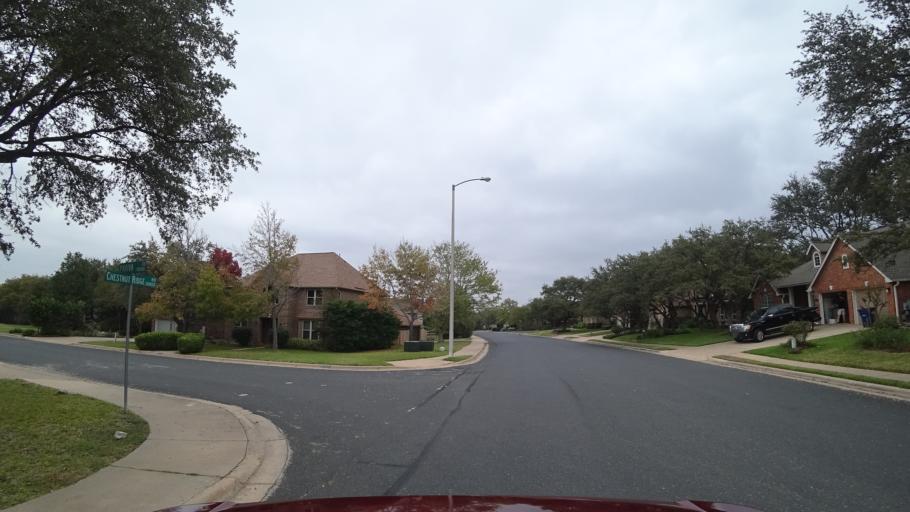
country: US
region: Texas
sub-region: Williamson County
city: Anderson Mill
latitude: 30.4367
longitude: -97.8216
